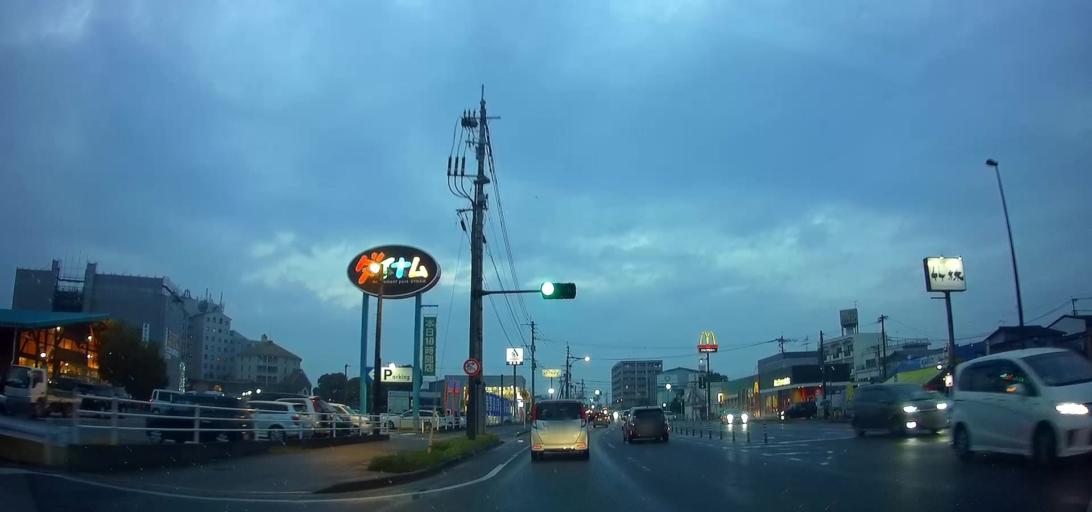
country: JP
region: Nagasaki
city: Omura
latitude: 32.9079
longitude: 129.9555
